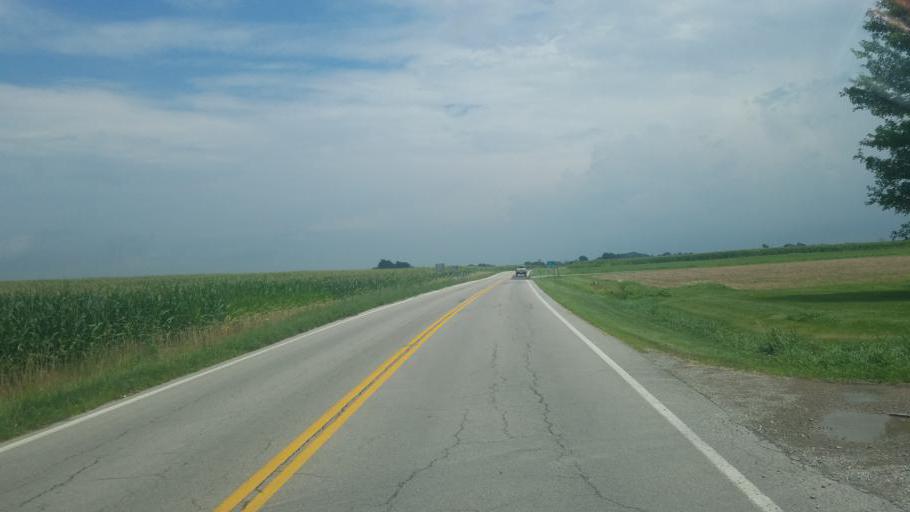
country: US
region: Ohio
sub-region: Champaign County
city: North Lewisburg
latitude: 40.4019
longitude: -83.5333
